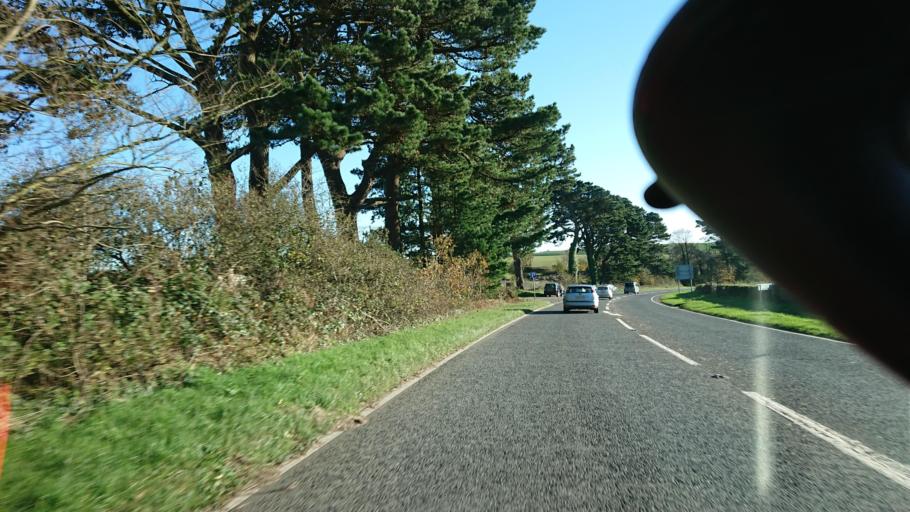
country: GB
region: England
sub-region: Cornwall
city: Pillaton
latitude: 50.4052
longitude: -4.3483
